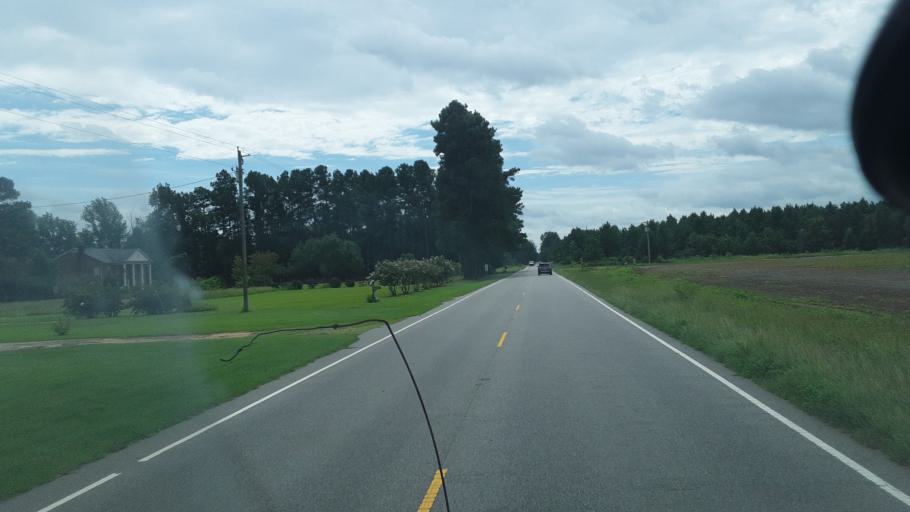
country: US
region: North Carolina
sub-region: Robeson County
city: Rowland
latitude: 34.6208
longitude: -79.3342
